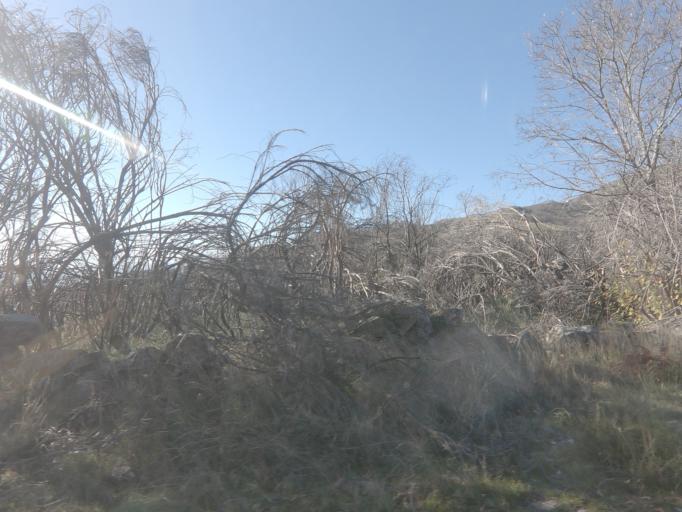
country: PT
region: Vila Real
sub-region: Vila Real
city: Vila Real
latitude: 41.3518
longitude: -7.7477
